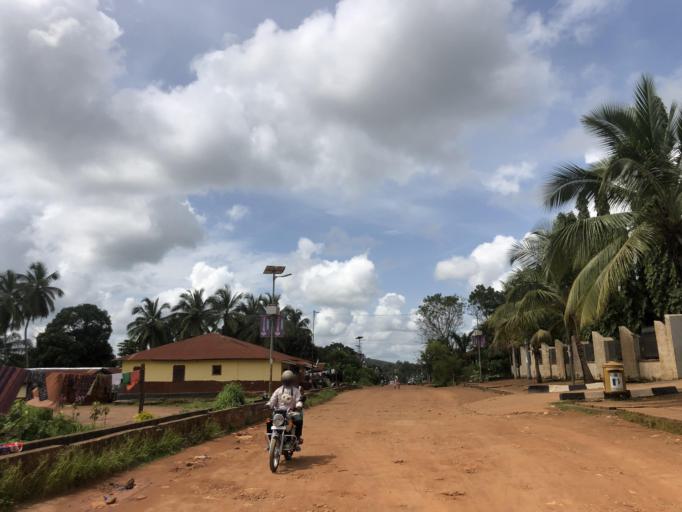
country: SL
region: Northern Province
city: Makeni
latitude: 8.8737
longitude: -12.0516
